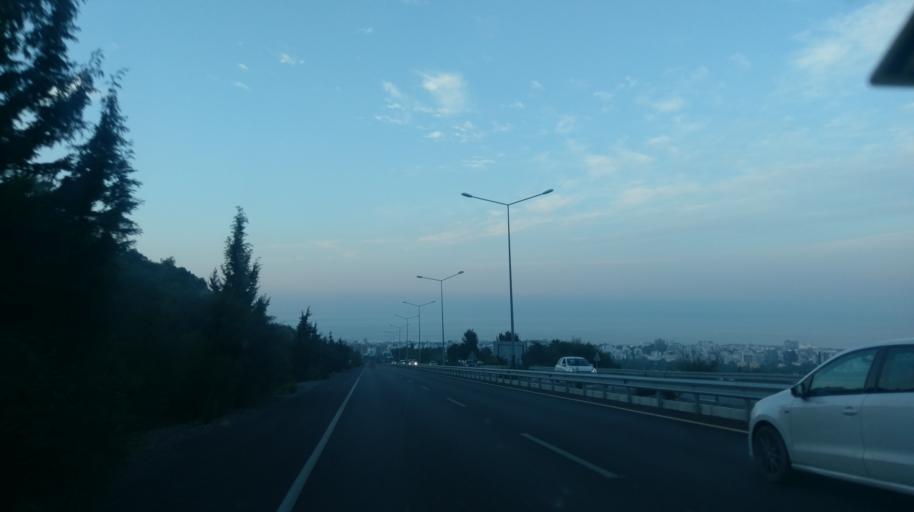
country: CY
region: Keryneia
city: Kyrenia
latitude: 35.3142
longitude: 33.3231
